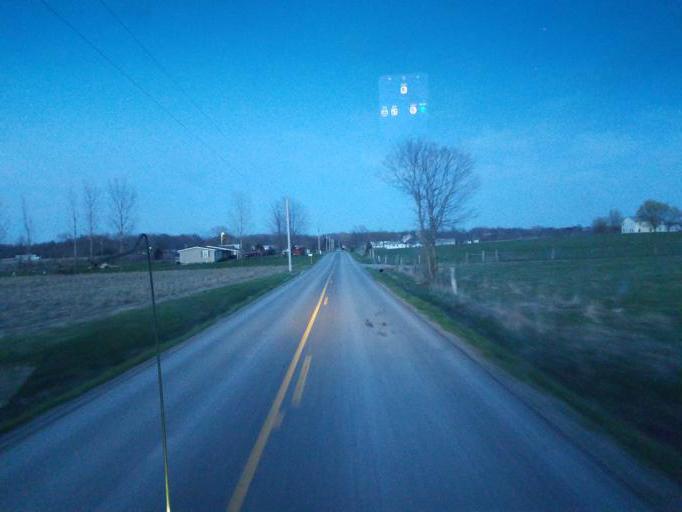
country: US
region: Ohio
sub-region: Logan County
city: De Graff
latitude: 40.3548
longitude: -83.9490
